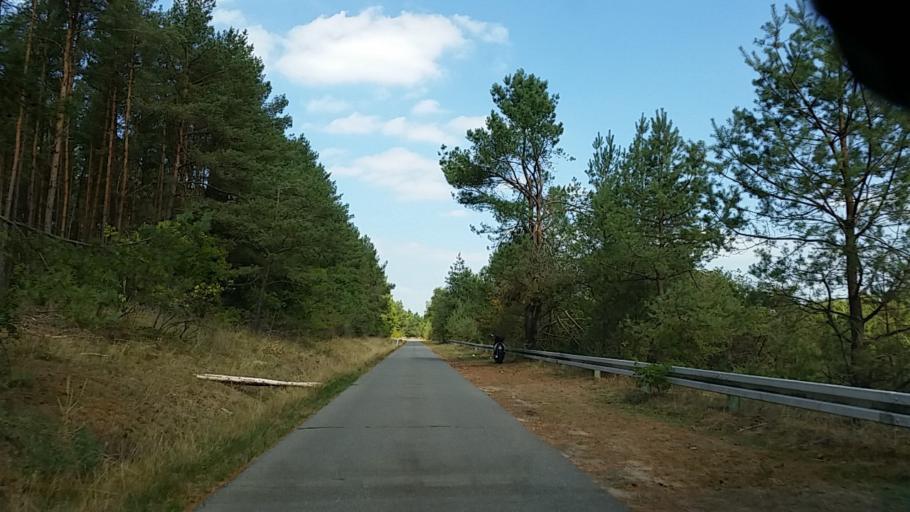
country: DE
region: Lower Saxony
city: Wendisch Evern
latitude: 53.2314
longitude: 10.4887
